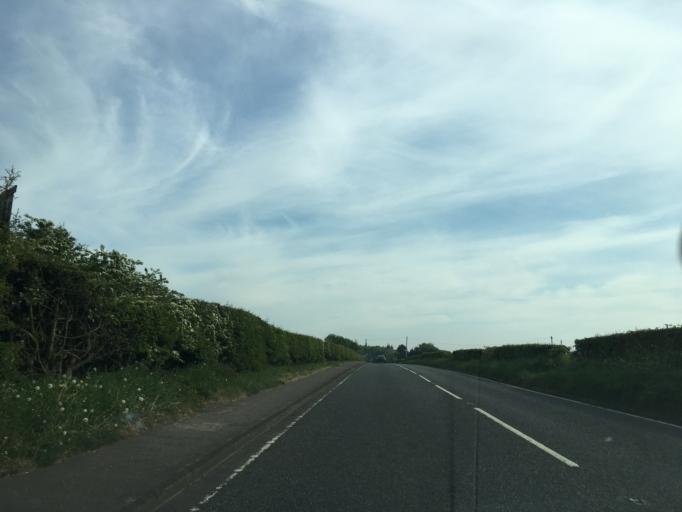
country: GB
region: Scotland
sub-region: Midlothian
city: Loanhead
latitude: 55.8776
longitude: -3.1926
